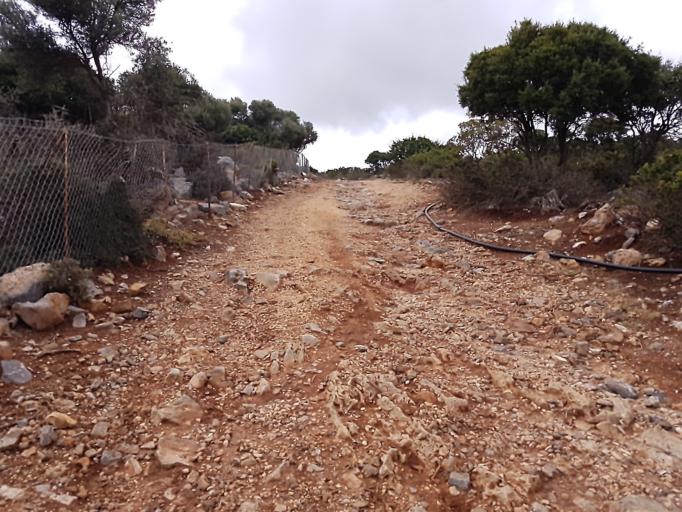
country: GR
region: Crete
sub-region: Nomos Irakleiou
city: Limin Khersonisou
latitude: 35.2927
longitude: 25.3787
